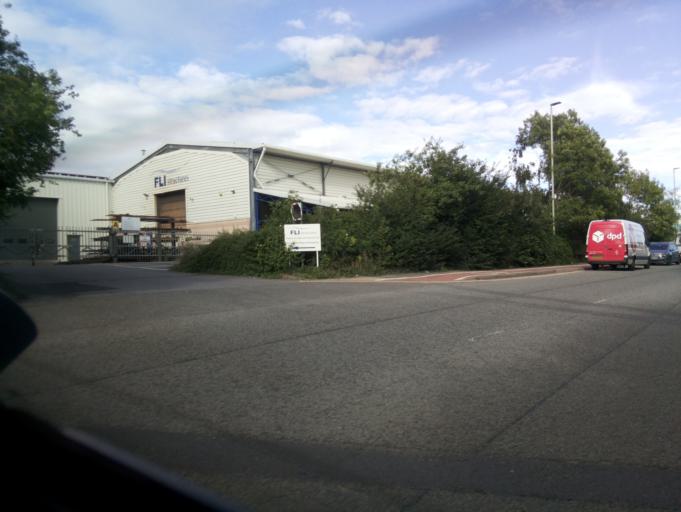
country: GB
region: England
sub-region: Gloucestershire
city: Gloucester
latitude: 51.8130
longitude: -2.2714
